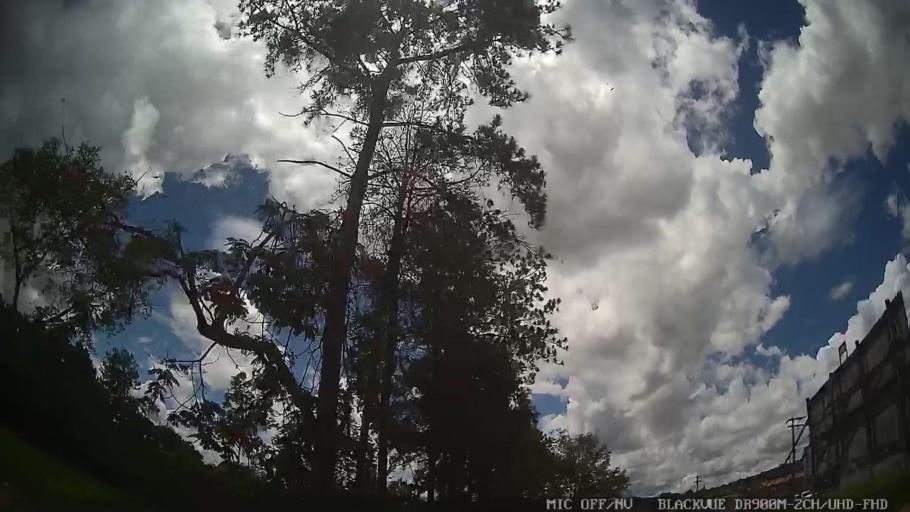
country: BR
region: Sao Paulo
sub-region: Jaguariuna
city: Jaguariuna
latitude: -22.6952
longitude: -46.9918
